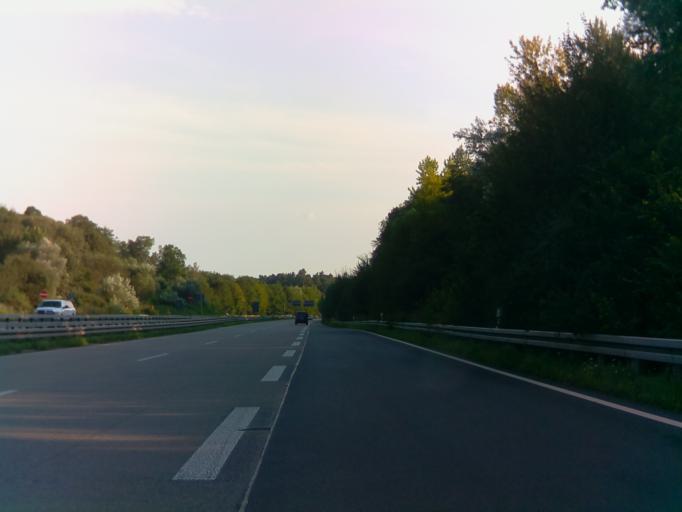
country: DE
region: Hesse
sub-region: Regierungsbezirk Darmstadt
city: Munster
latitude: 49.9040
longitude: 8.8682
